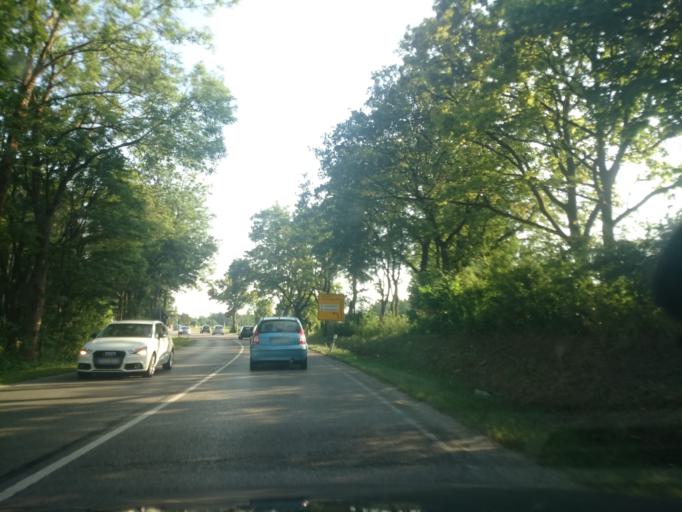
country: DE
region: Bavaria
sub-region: Upper Bavaria
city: Gilching
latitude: 48.0921
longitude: 11.2807
